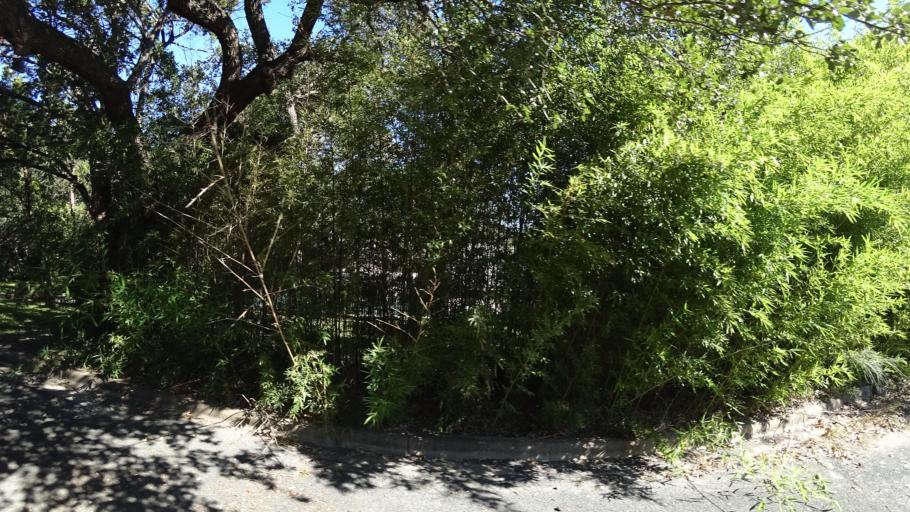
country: US
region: Texas
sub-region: Travis County
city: West Lake Hills
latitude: 30.3164
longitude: -97.7949
